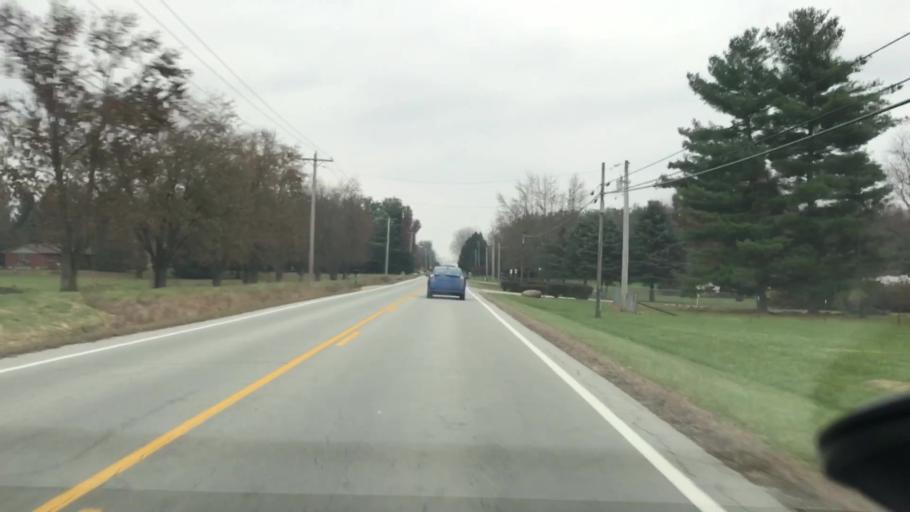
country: US
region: Ohio
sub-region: Clark County
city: Holiday Valley
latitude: 39.7899
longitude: -83.9588
